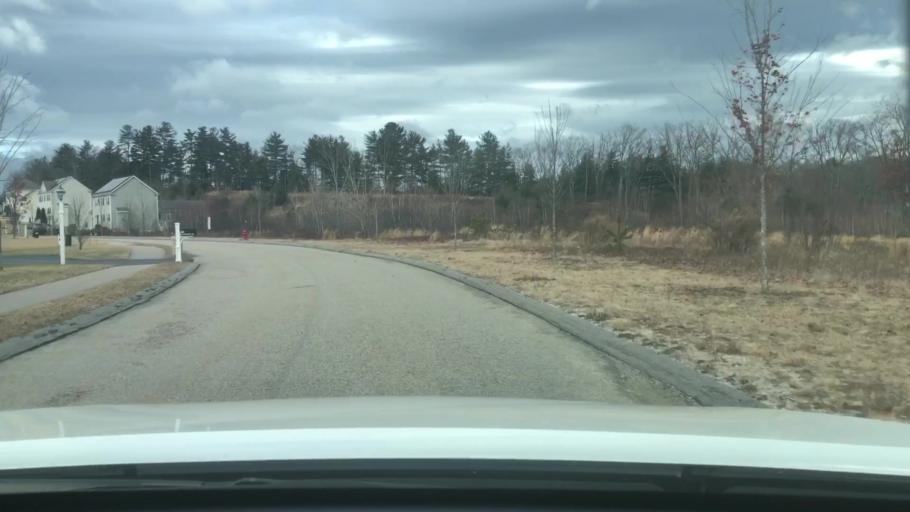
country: US
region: Rhode Island
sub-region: Providence County
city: Woonsocket
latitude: 42.0360
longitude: -71.5091
